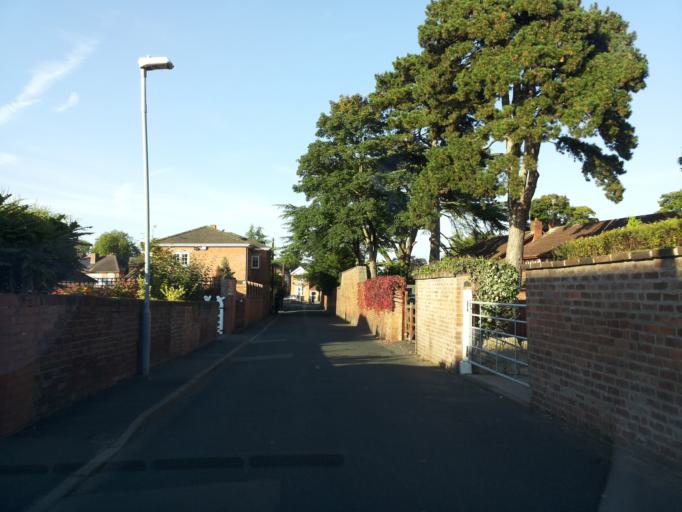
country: GB
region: England
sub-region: Worcestershire
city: Stourport-on-Severn
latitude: 52.3409
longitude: -2.2833
